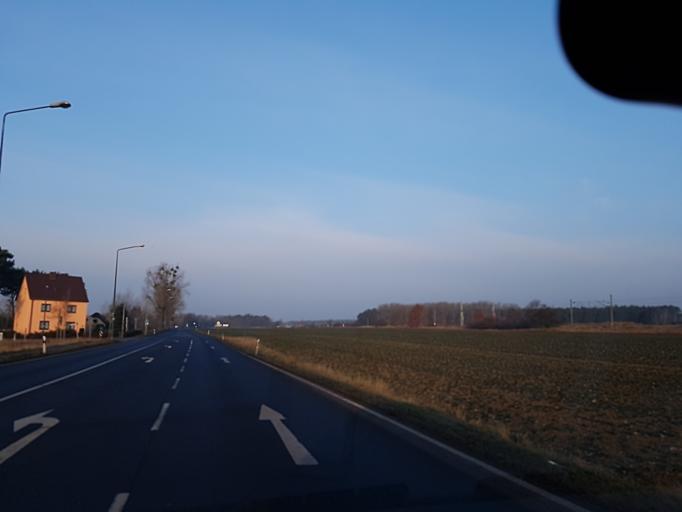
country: DE
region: Saxony-Anhalt
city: Nudersdorf
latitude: 51.8779
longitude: 12.5358
